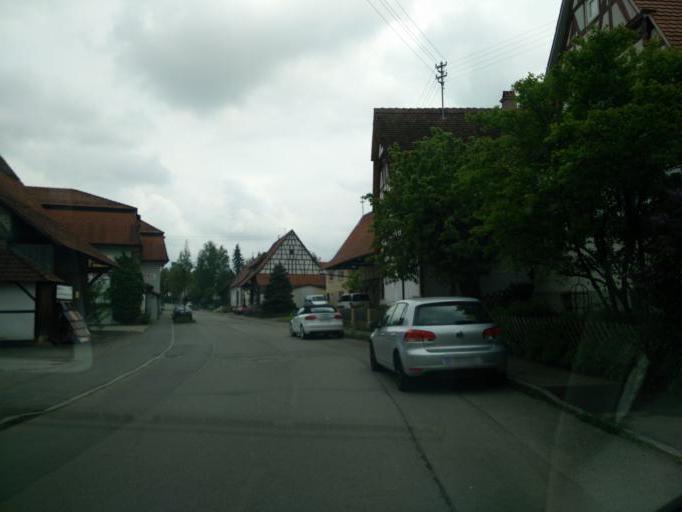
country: DE
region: Baden-Wuerttemberg
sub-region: Tuebingen Region
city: Gomaringen
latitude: 48.4858
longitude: 9.1102
